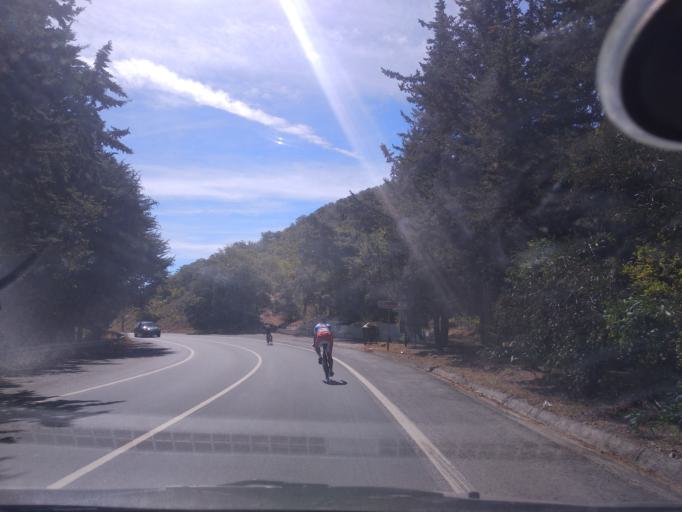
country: PT
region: Faro
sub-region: Sao Bras de Alportel
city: Sao Bras de Alportel
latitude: 37.1554
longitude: -7.8397
